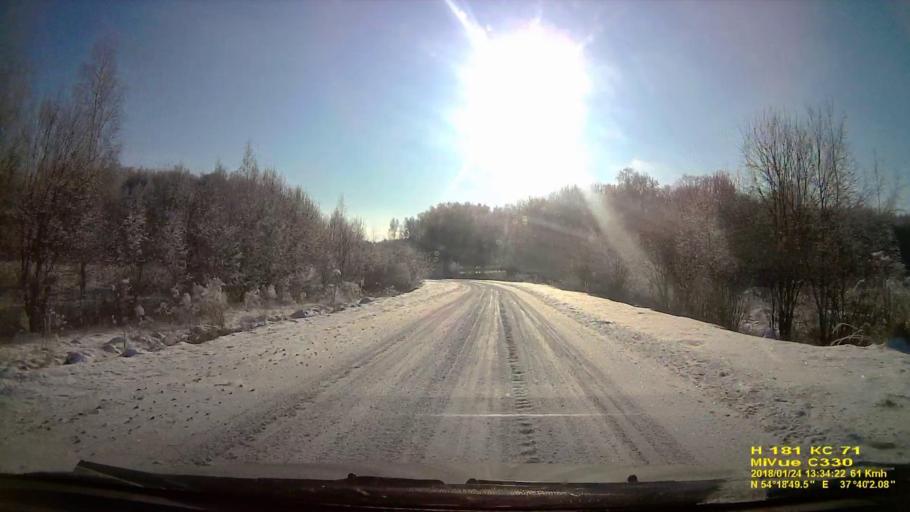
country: RU
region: Tula
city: Revyakino
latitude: 54.3136
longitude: 37.6672
